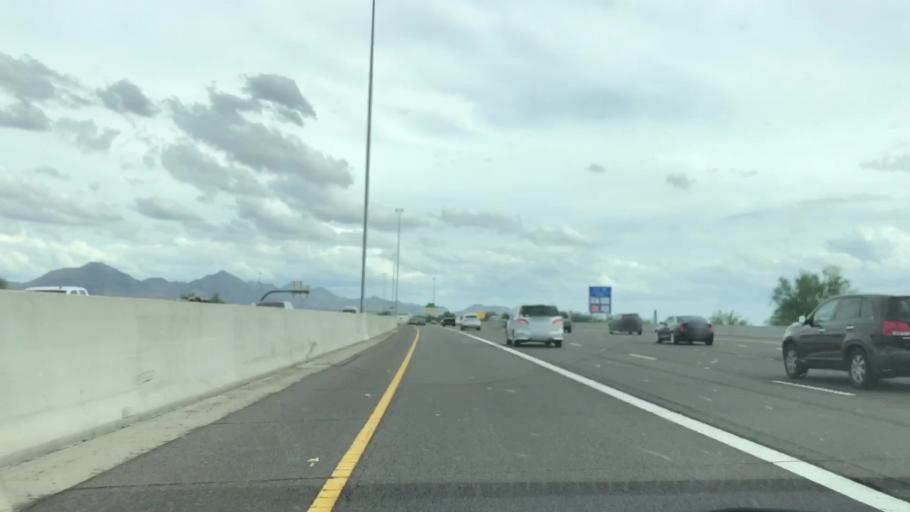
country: US
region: Arizona
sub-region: Maricopa County
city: Paradise Valley
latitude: 33.6636
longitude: -111.9516
